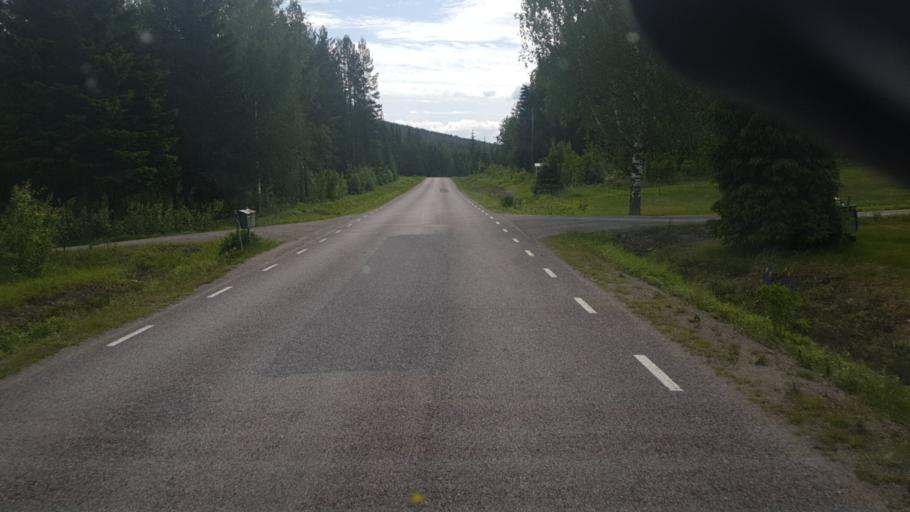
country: SE
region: Vaermland
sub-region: Eda Kommun
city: Charlottenberg
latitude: 59.9502
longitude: 12.3854
